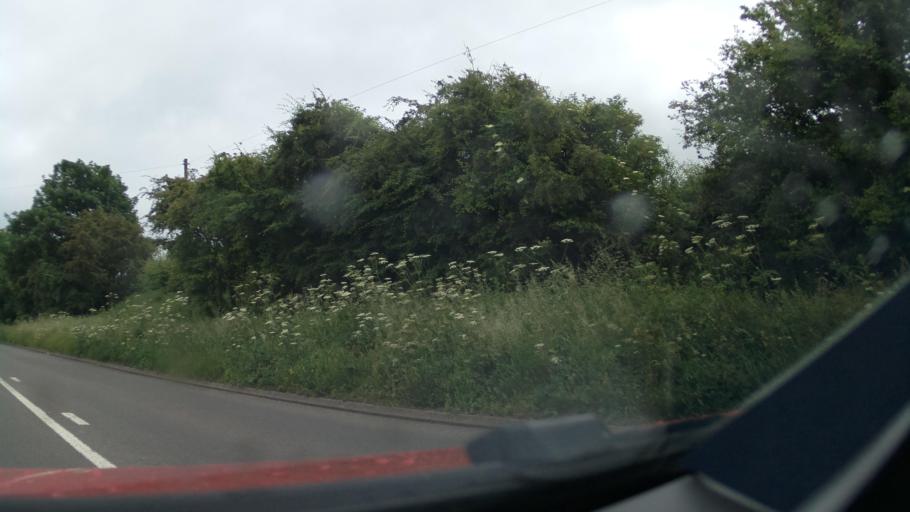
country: GB
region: England
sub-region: Staffordshire
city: Burton upon Trent
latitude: 52.8446
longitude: -1.6751
